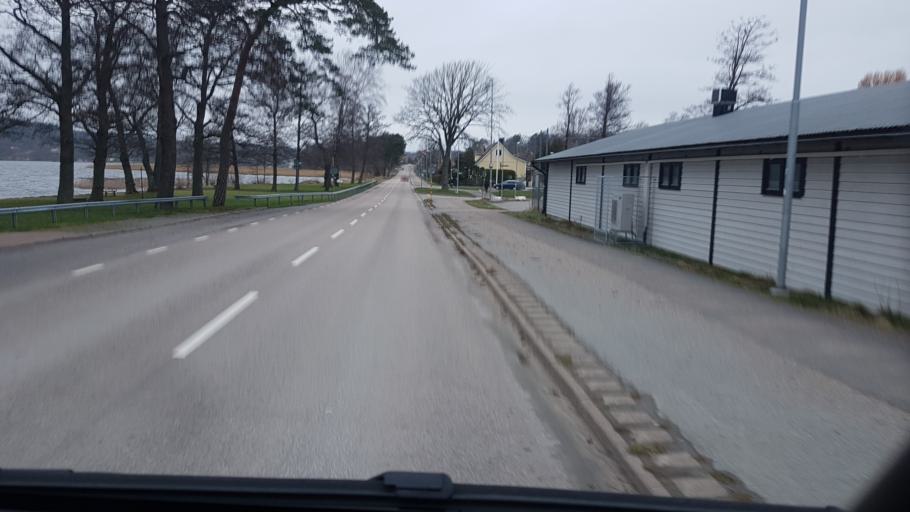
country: SE
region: Vaestra Goetaland
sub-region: Lerums Kommun
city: Lerum
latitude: 57.7680
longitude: 12.2528
